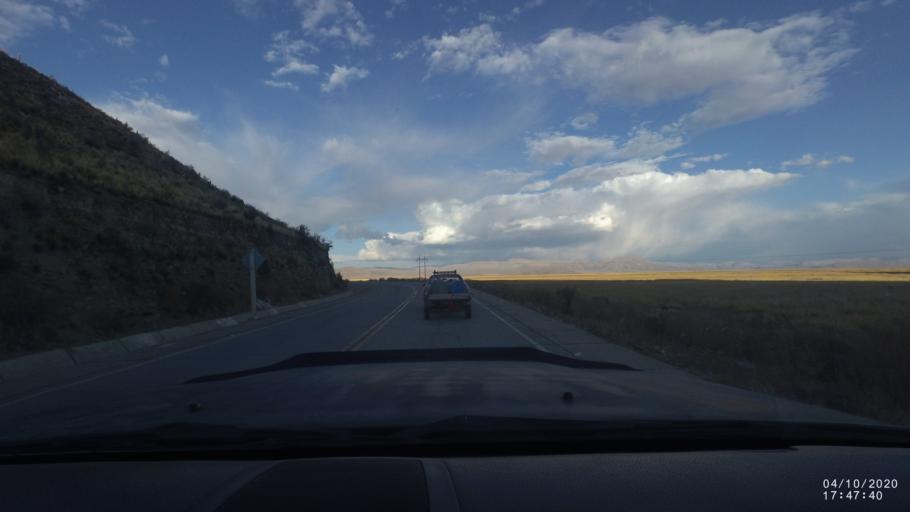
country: BO
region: Oruro
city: Oruro
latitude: -18.0228
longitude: -67.1421
